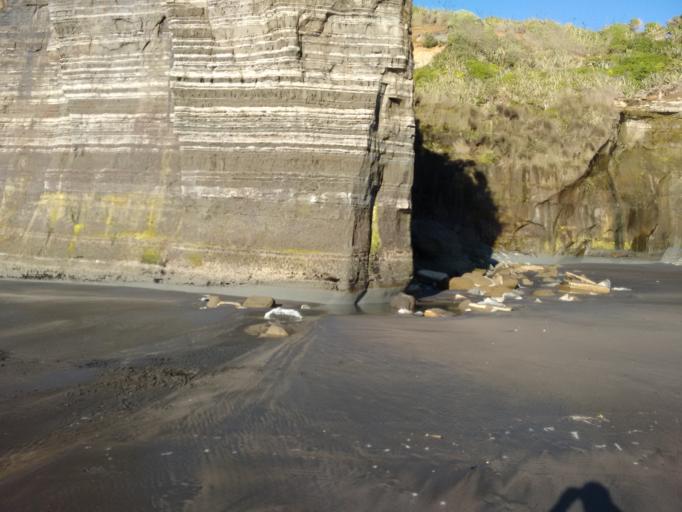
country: NZ
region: Taranaki
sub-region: New Plymouth District
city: Waitara
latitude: -38.8199
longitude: 174.5807
